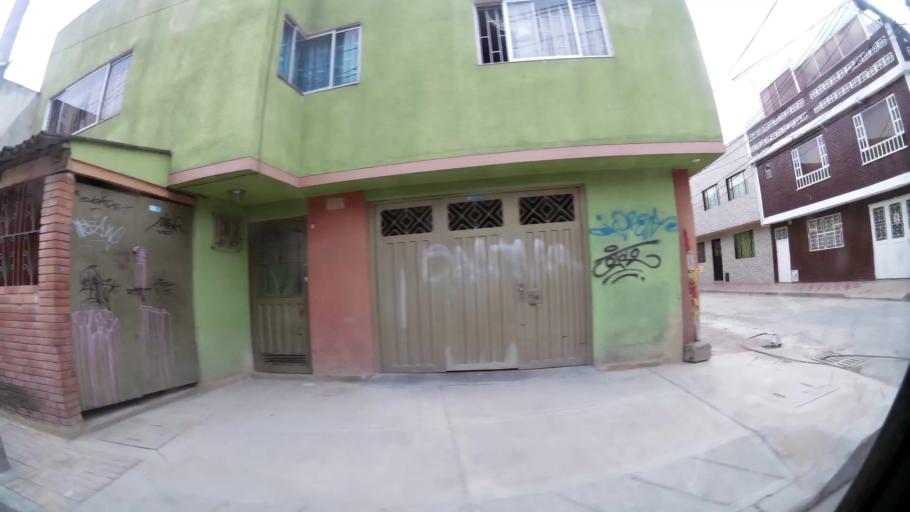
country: CO
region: Cundinamarca
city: Funza
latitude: 4.7126
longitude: -74.2182
